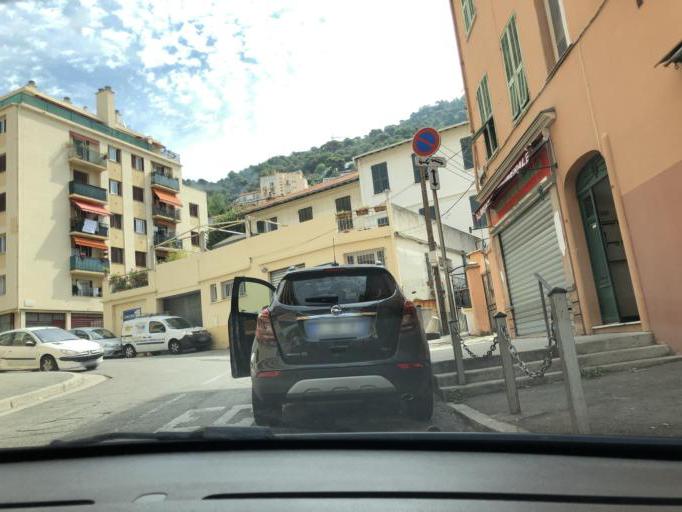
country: FR
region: Provence-Alpes-Cote d'Azur
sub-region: Departement des Alpes-Maritimes
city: Villefranche-sur-Mer
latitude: 43.7167
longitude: 7.2946
